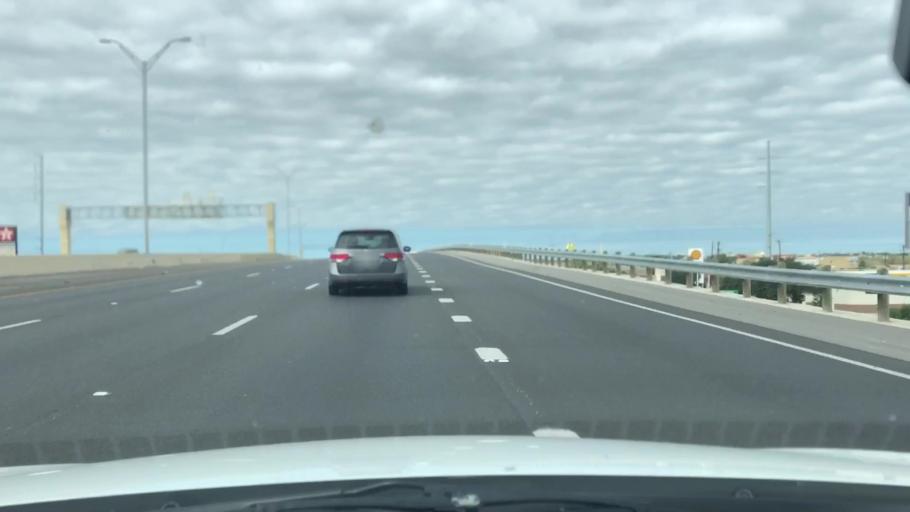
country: US
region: Texas
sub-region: Bexar County
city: Leon Valley
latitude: 29.4417
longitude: -98.6620
